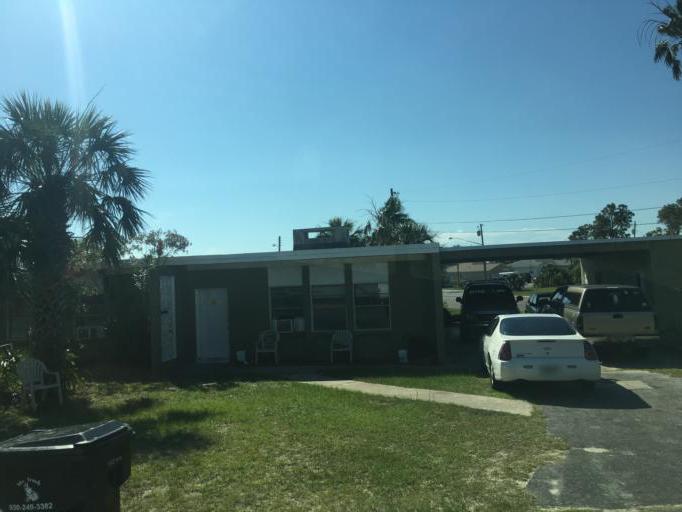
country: US
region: Florida
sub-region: Bay County
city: Panama City Beach
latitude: 30.1985
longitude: -85.8406
